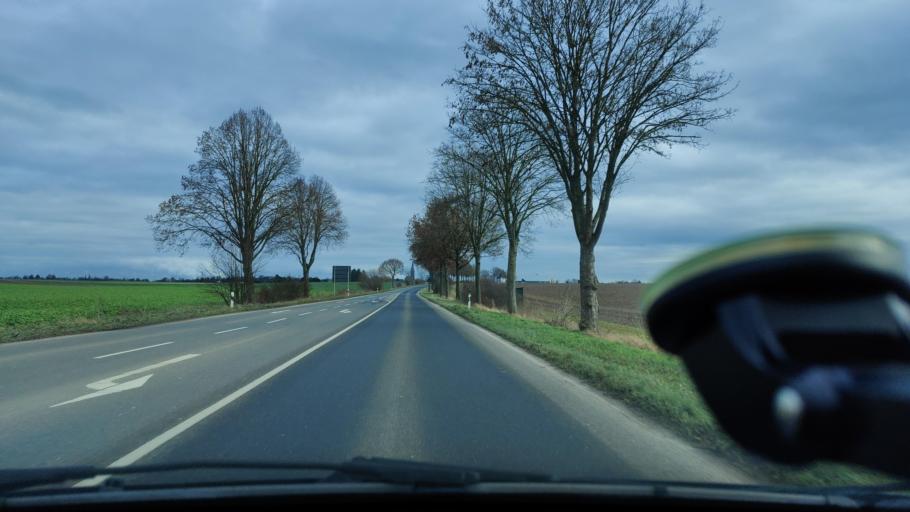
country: DE
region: North Rhine-Westphalia
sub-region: Regierungsbezirk Koln
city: Titz
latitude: 51.0077
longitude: 6.4064
